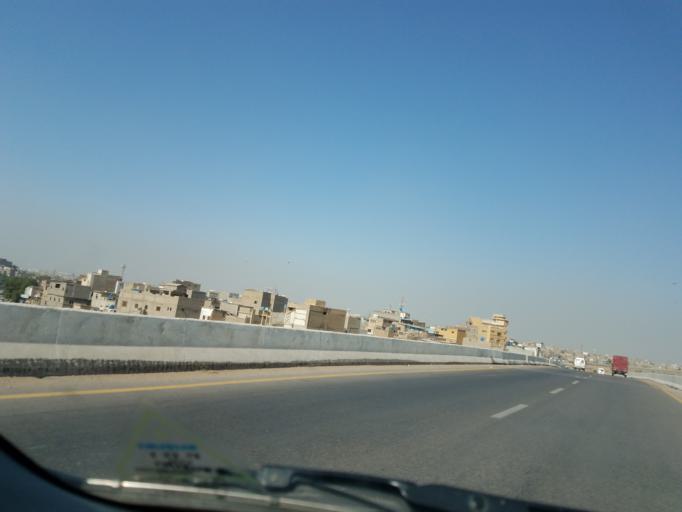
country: PK
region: Sindh
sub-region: Karachi District
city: Karachi
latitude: 24.8845
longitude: 67.0211
